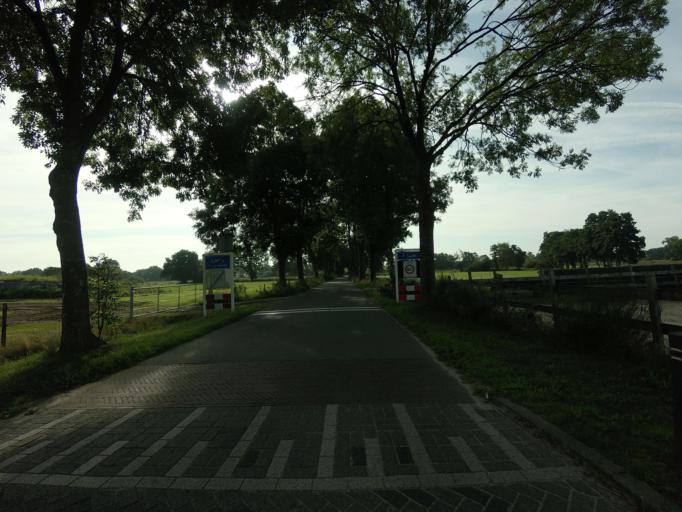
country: NL
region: Drenthe
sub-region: Gemeente Assen
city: Assen
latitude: 53.0099
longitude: 6.6153
